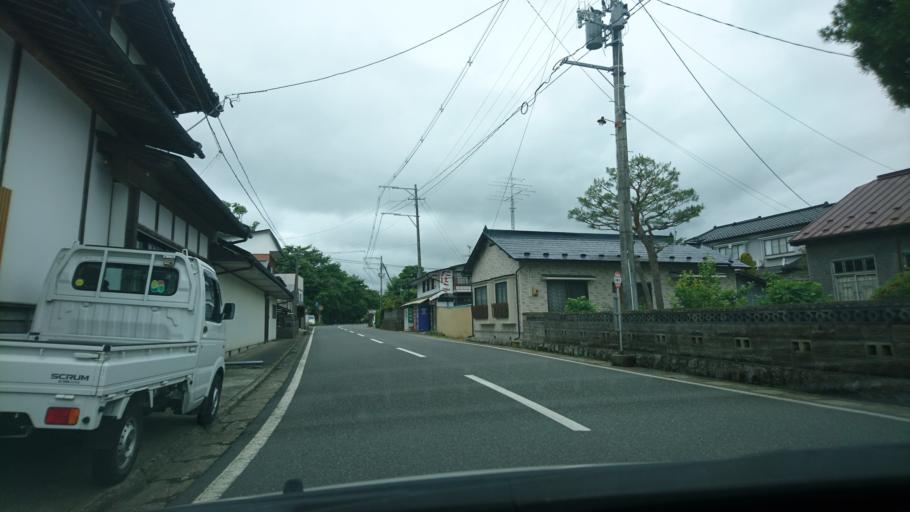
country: JP
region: Iwate
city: Ichinoseki
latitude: 38.9428
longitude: 141.0535
